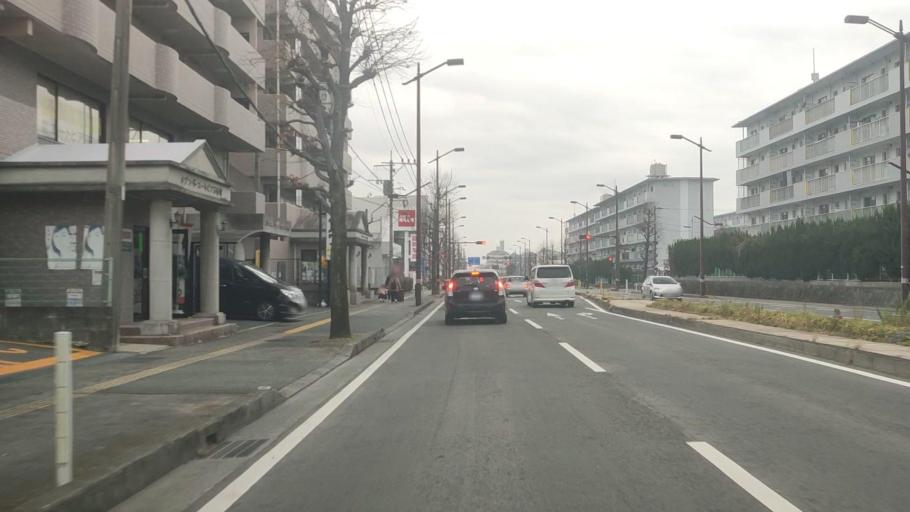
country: JP
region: Kumamoto
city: Kumamoto
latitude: 32.8112
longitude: 130.7732
